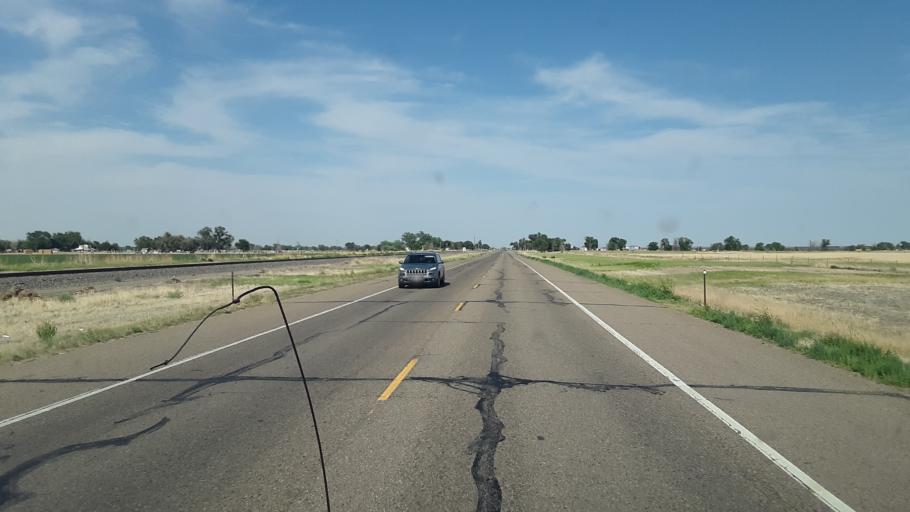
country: US
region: Colorado
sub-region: Bent County
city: Las Animas
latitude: 38.0601
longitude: -103.2868
